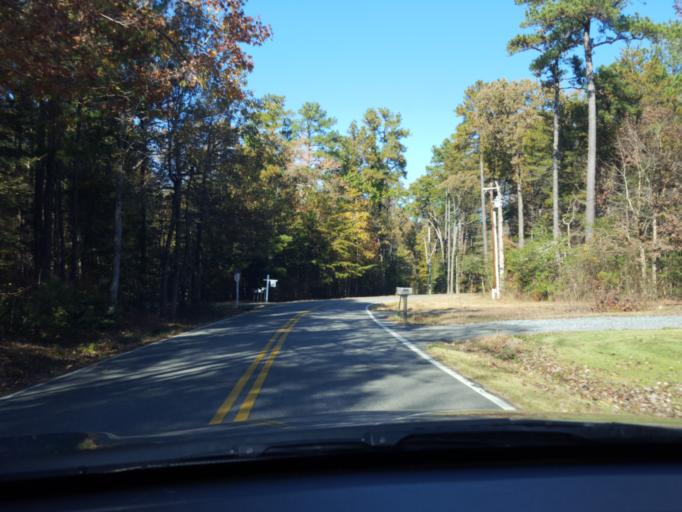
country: US
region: Maryland
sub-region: Saint Mary's County
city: California
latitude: 38.2429
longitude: -76.5435
